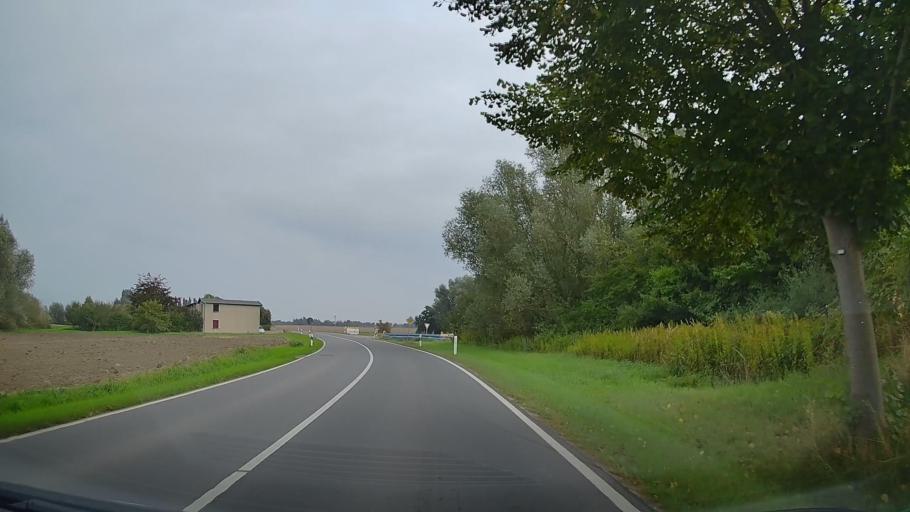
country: DE
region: Mecklenburg-Vorpommern
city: Ostseebad Kuhlungsborn
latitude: 54.1350
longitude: 11.7608
